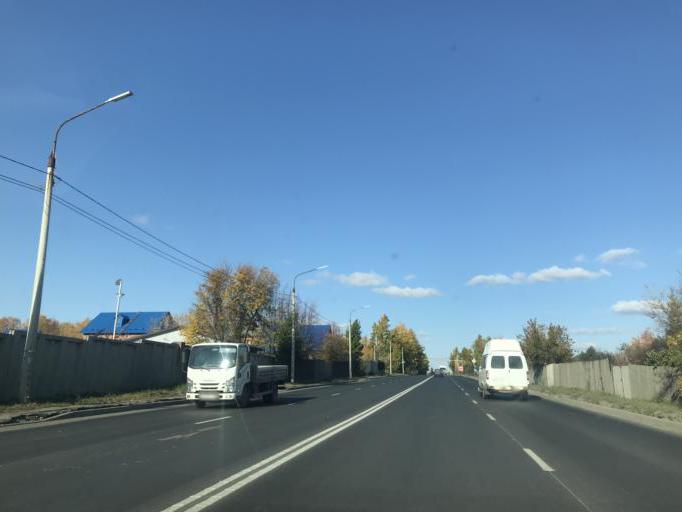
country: RU
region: Chelyabinsk
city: Roshchino
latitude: 55.2360
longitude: 61.3171
